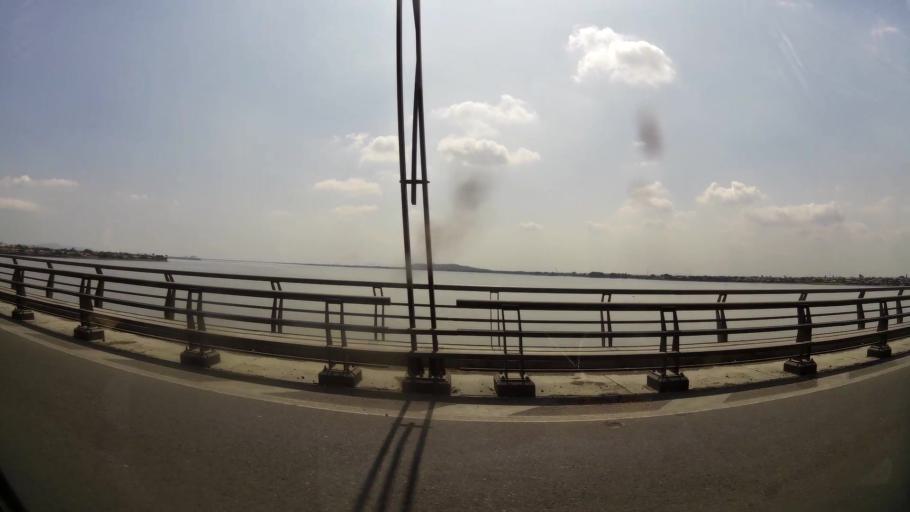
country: EC
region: Guayas
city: Eloy Alfaro
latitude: -2.1580
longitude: -79.8554
